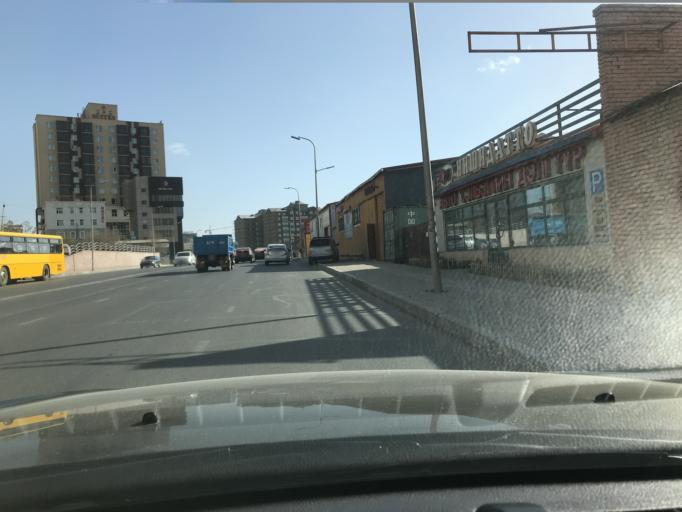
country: MN
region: Ulaanbaatar
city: Ulaanbaatar
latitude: 47.9250
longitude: 106.9462
